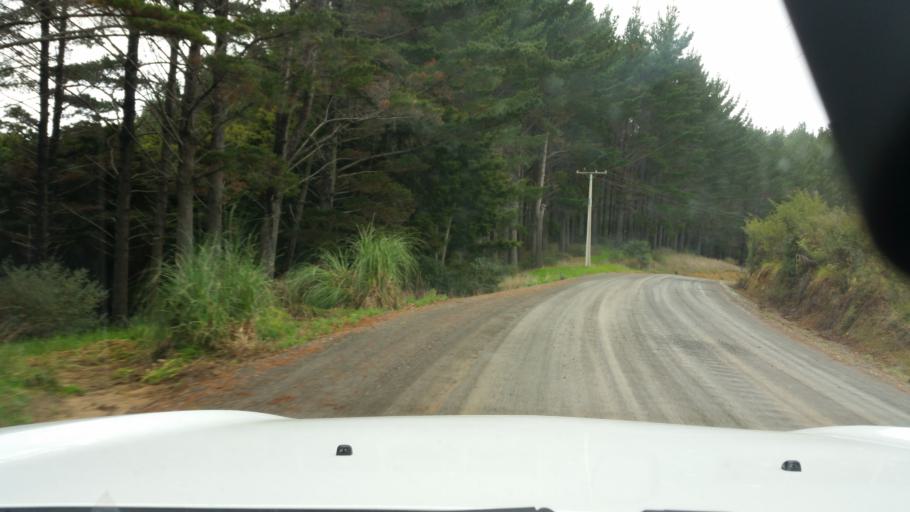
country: NZ
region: Northland
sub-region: Whangarei
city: Ngunguru
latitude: -35.7461
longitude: 174.4890
